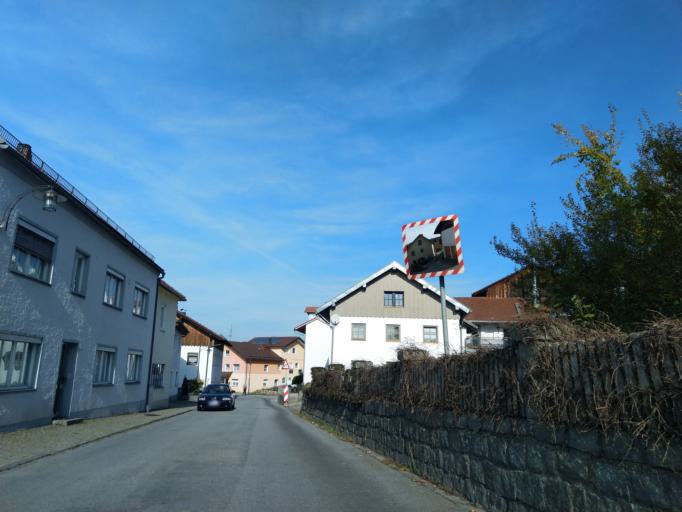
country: DE
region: Bavaria
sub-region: Lower Bavaria
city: Grattersdorf
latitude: 48.8028
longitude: 13.1541
